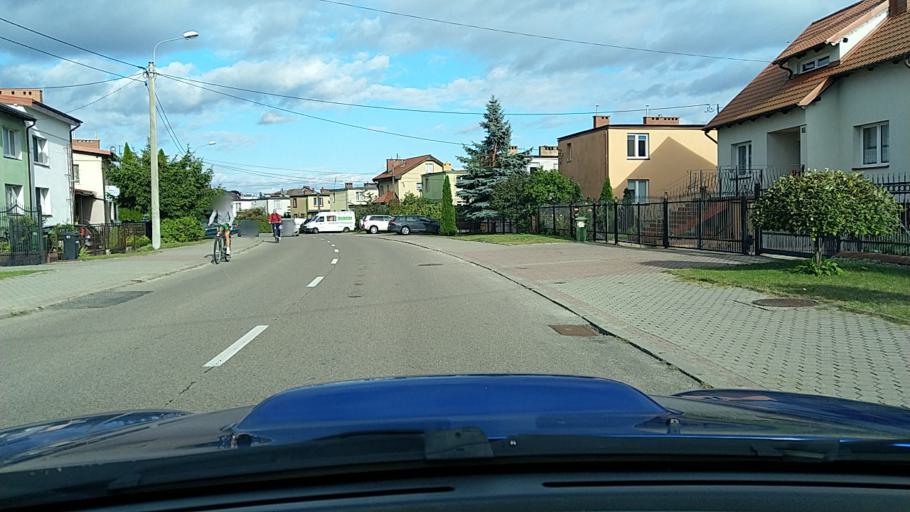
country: PL
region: Warmian-Masurian Voivodeship
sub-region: Olsztyn
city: Kortowo
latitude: 53.7660
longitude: 20.4337
